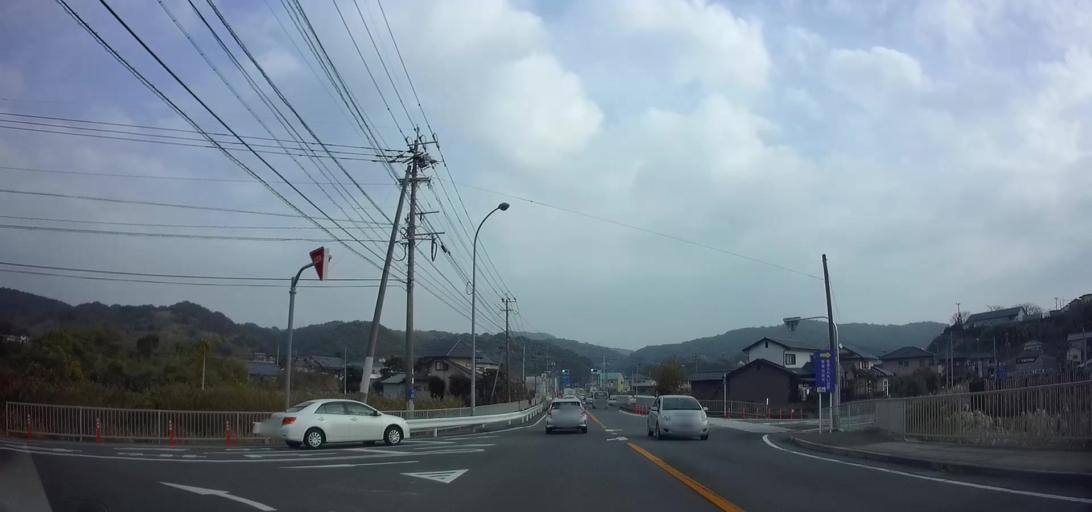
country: JP
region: Nagasaki
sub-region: Isahaya-shi
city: Isahaya
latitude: 32.7957
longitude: 130.0797
